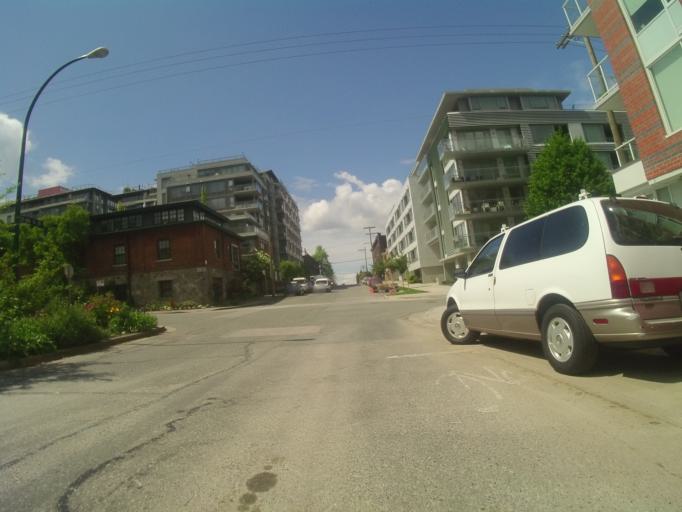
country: CA
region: British Columbia
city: Vancouver
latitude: 49.2655
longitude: -123.0984
